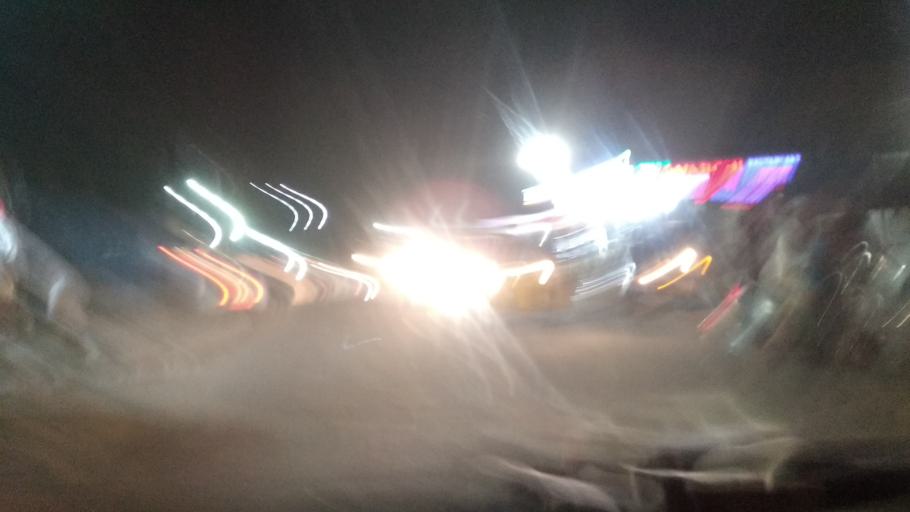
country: IN
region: Telangana
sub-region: Rangareddi
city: Kukatpalli
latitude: 17.4540
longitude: 78.4197
